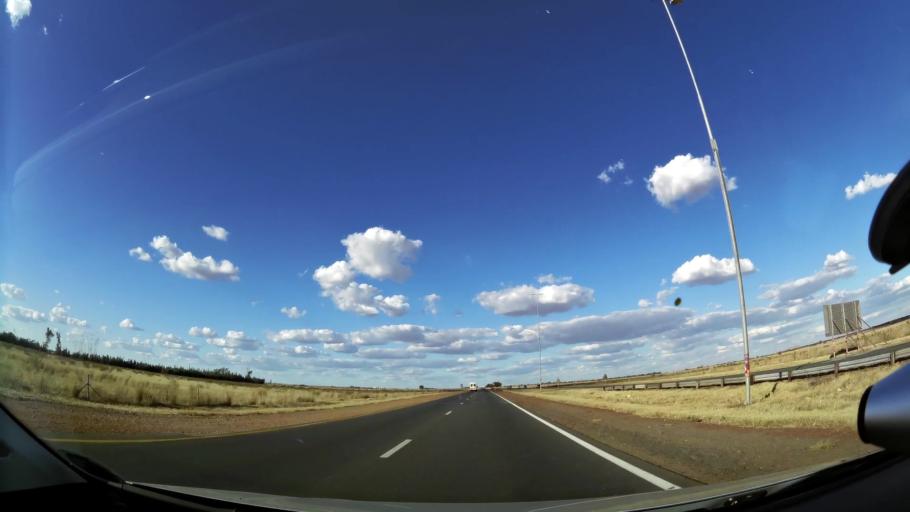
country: ZA
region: North-West
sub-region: Dr Kenneth Kaunda District Municipality
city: Klerksdorp
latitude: -26.8471
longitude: 26.7107
